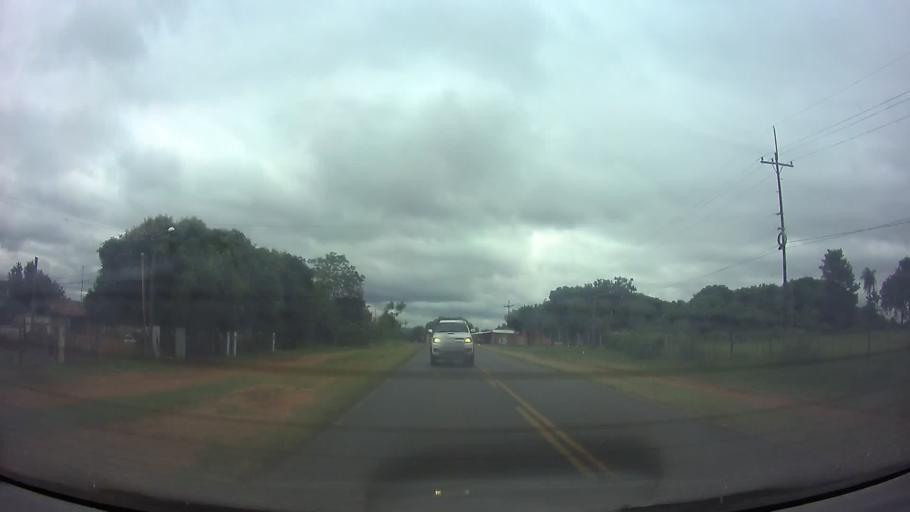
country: PY
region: Central
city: Guarambare
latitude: -25.5194
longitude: -57.4914
